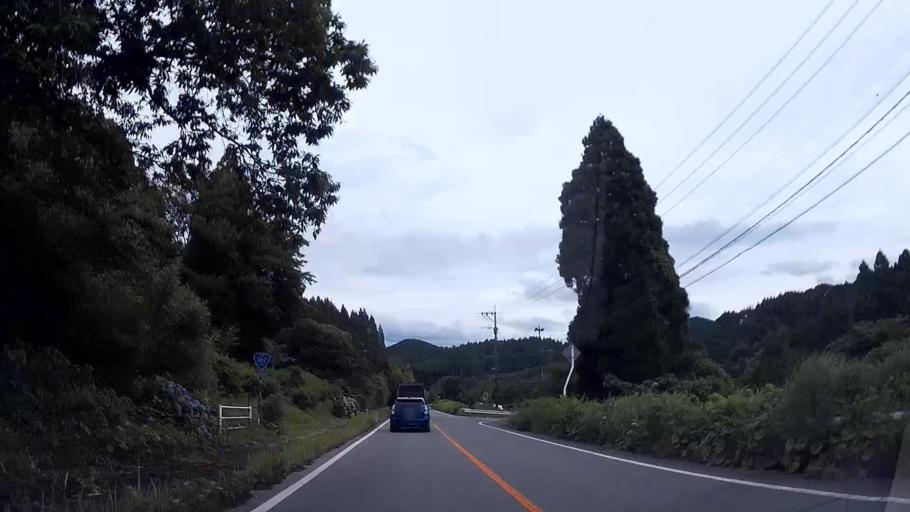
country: JP
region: Kumamoto
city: Aso
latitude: 33.1226
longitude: 131.0215
